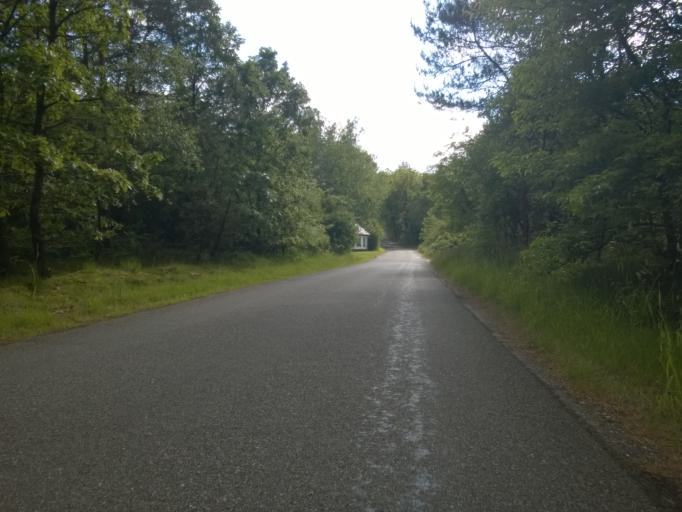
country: DK
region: Central Jutland
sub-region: Holstebro Kommune
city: Vinderup
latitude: 56.5159
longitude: 8.8437
